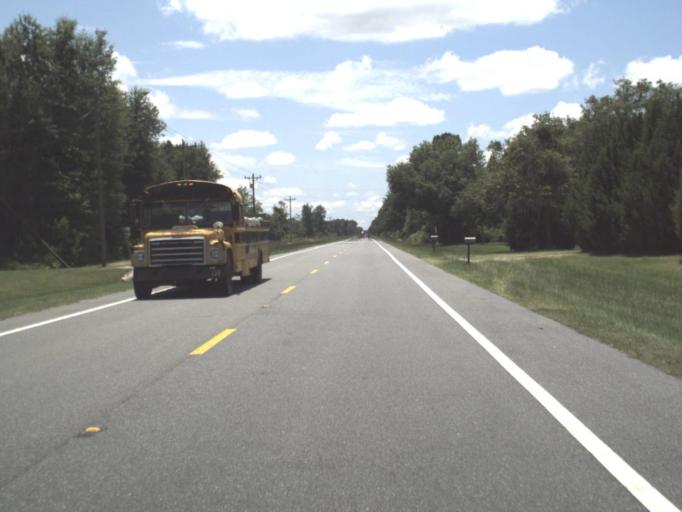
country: US
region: Florida
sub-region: Lafayette County
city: Mayo
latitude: 29.9210
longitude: -82.9509
